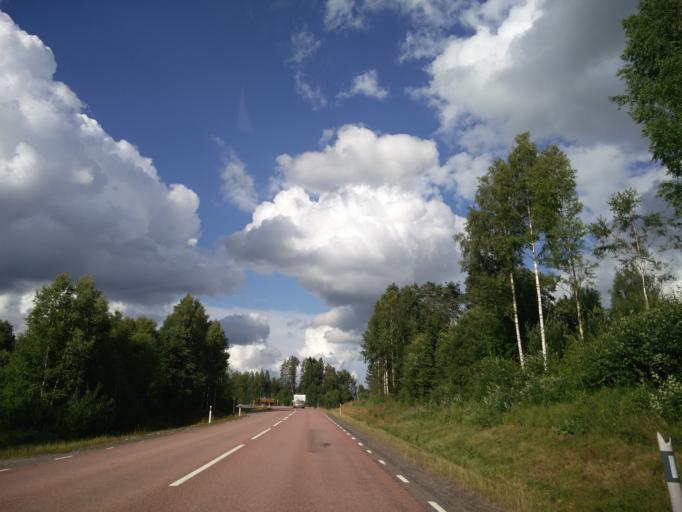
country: SE
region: Vaermland
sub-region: Torsby Kommun
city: Torsby
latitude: 60.2551
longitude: 13.0213
